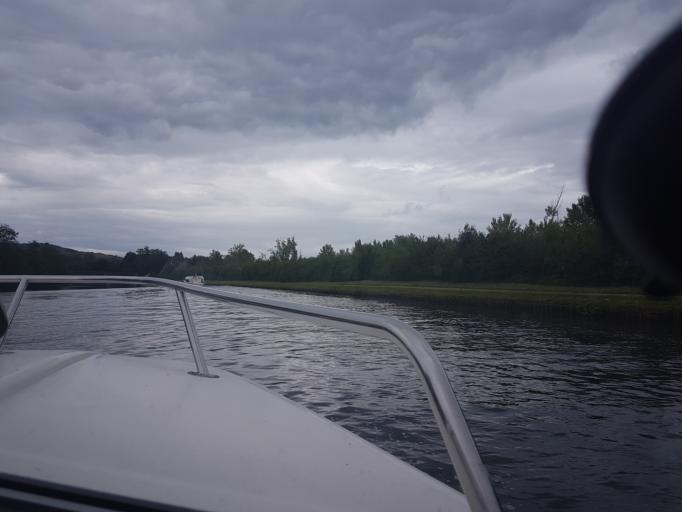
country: FR
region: Bourgogne
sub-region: Departement de l'Yonne
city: Champs-sur-Yonne
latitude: 47.7258
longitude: 3.6093
